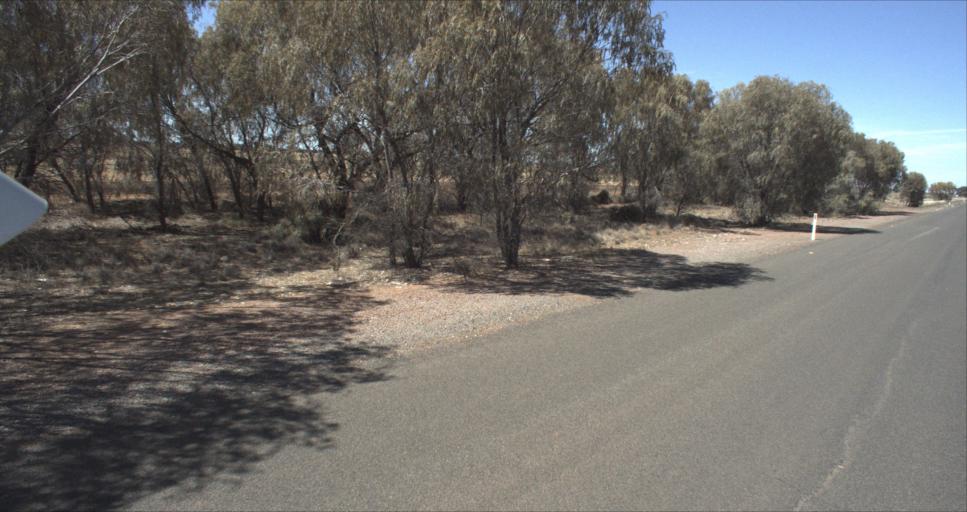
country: AU
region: New South Wales
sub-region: Leeton
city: Leeton
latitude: -34.4864
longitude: 146.2896
